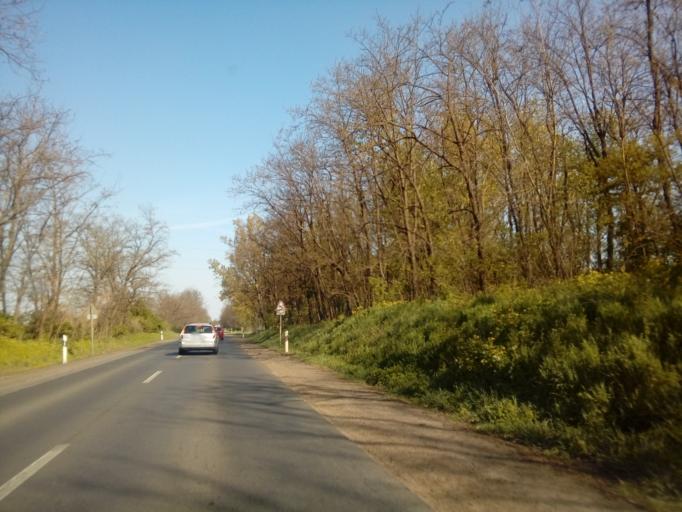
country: HU
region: Szabolcs-Szatmar-Bereg
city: Nyiregyhaza
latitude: 47.9178
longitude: 21.7712
